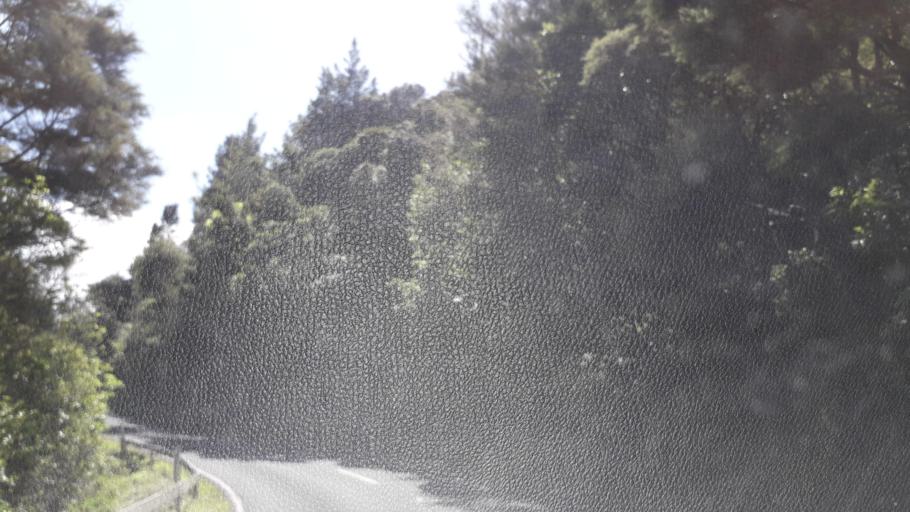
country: NZ
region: Northland
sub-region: Far North District
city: Paihia
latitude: -35.2530
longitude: 174.2631
